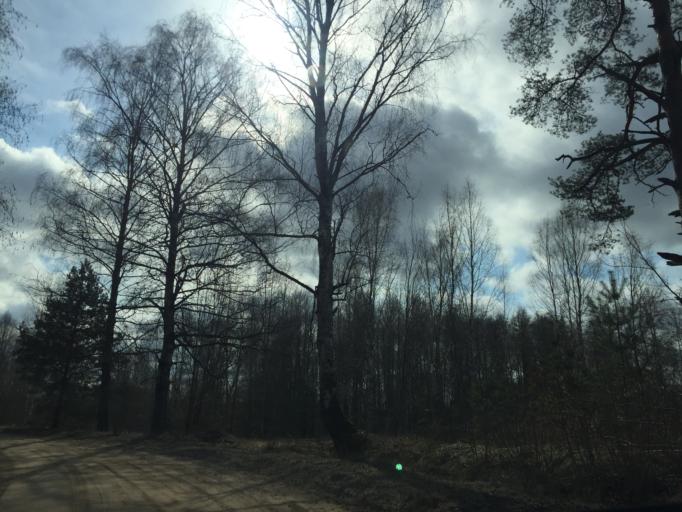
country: LV
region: Vecumnieki
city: Vecumnieki
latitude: 56.5845
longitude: 24.5816
